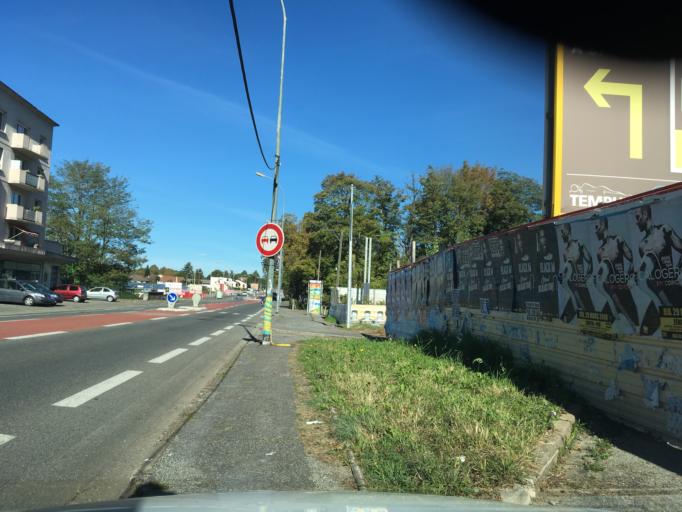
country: FR
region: Aquitaine
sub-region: Departement des Pyrenees-Atlantiques
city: Lons
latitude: 43.3267
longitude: -0.3795
